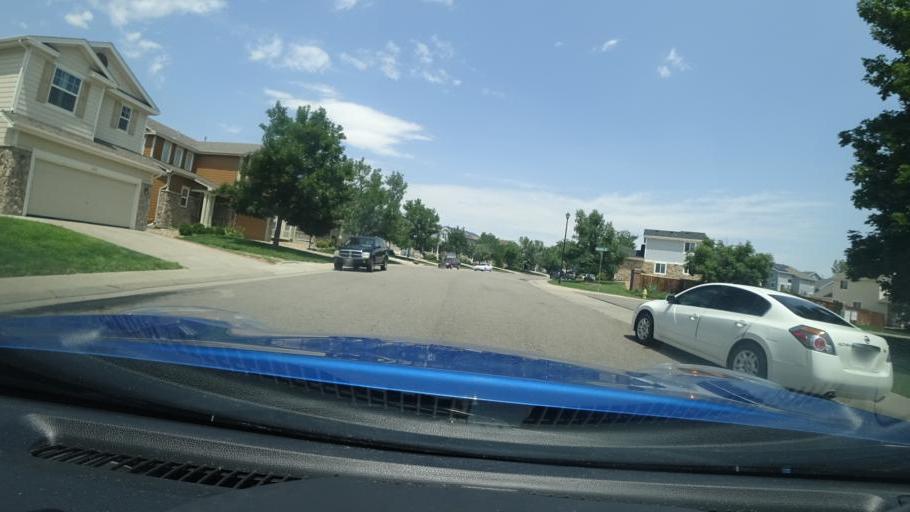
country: US
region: Colorado
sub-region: Adams County
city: Aurora
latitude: 39.6721
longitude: -104.7576
